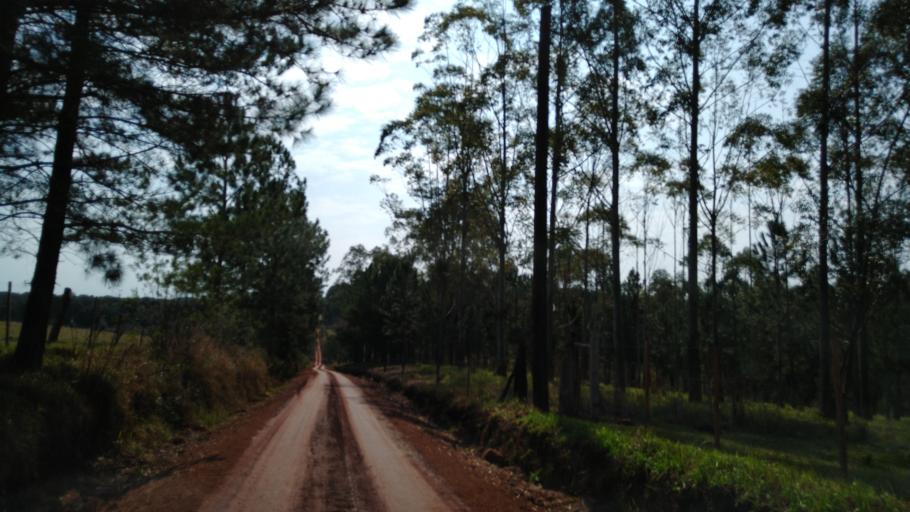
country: AR
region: Misiones
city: Capiovi
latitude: -26.9486
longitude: -55.0441
